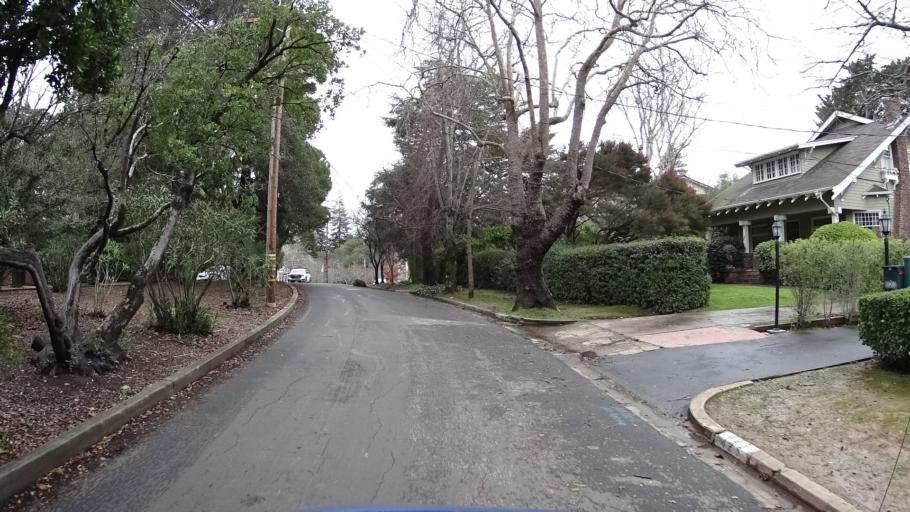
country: US
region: California
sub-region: San Mateo County
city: San Mateo
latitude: 37.5653
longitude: -122.3476
